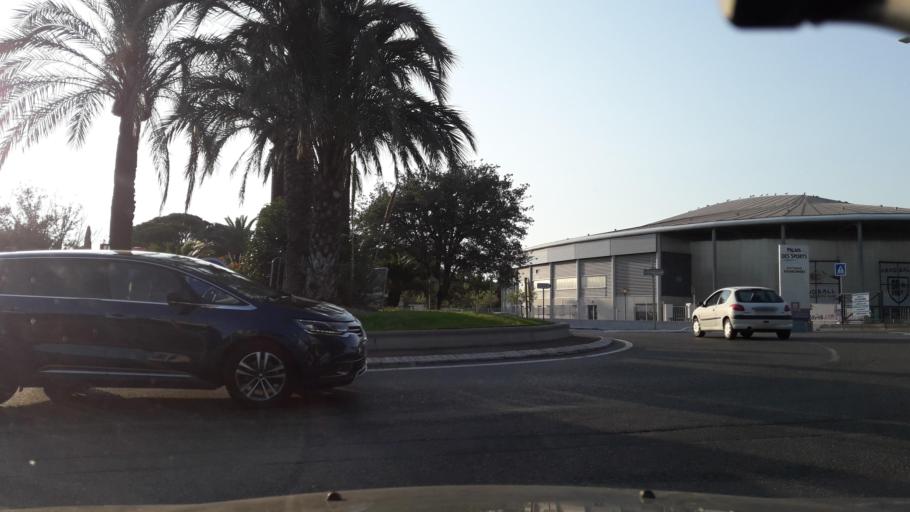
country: FR
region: Provence-Alpes-Cote d'Azur
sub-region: Departement du Var
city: Saint-Raphael
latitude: 43.4372
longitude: 6.7694
